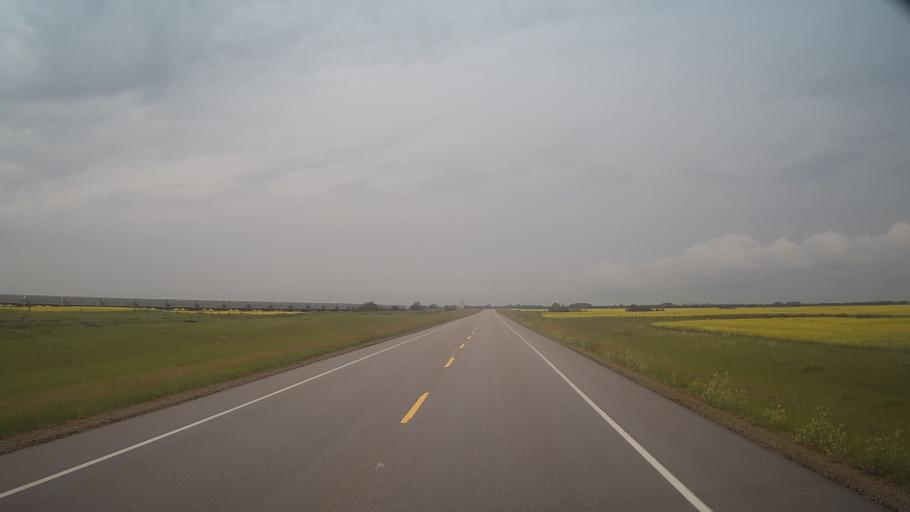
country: CA
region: Saskatchewan
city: Wilkie
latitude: 52.3024
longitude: -108.6768
